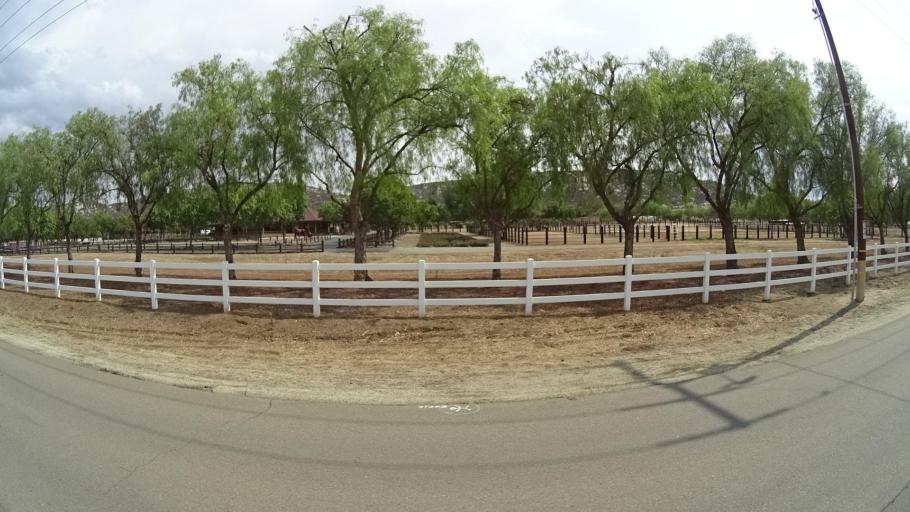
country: US
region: California
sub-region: San Diego County
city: Ramona
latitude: 33.0599
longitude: -116.8451
